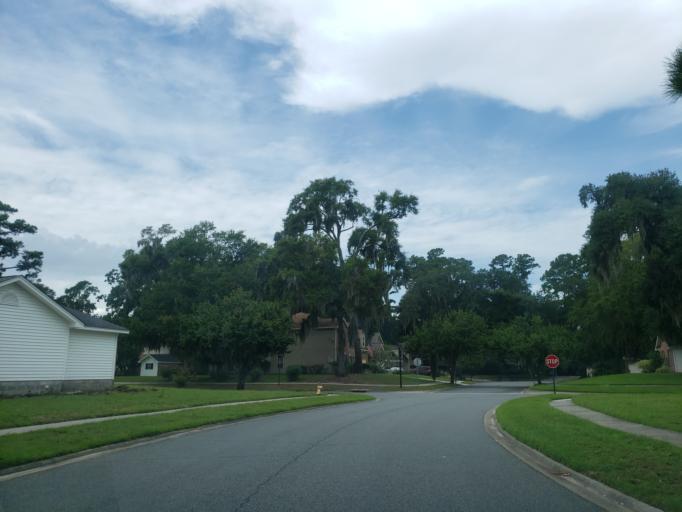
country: US
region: Georgia
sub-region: Chatham County
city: Wilmington Island
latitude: 31.9961
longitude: -80.9768
